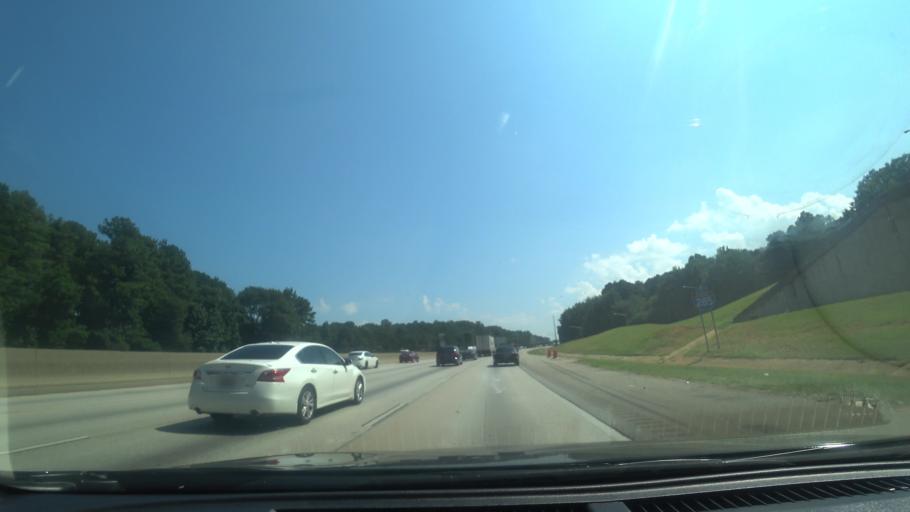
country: US
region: Georgia
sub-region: DeKalb County
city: Avondale Estates
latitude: 33.7694
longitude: -84.2329
